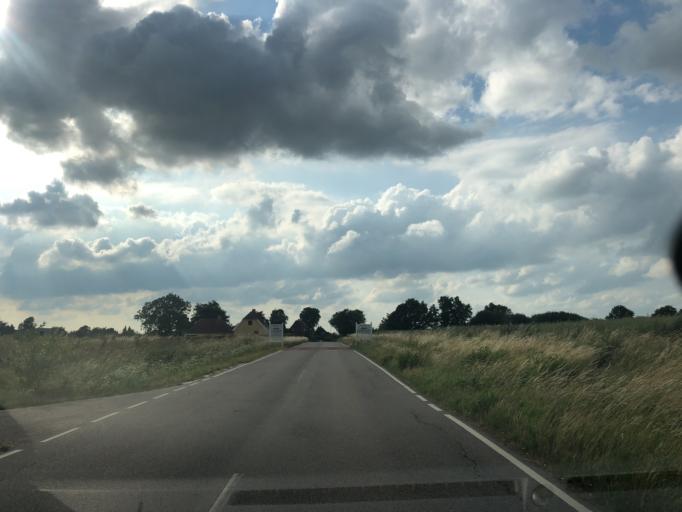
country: DK
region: Zealand
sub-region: Faxe Kommune
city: Haslev
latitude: 55.3147
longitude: 11.9819
